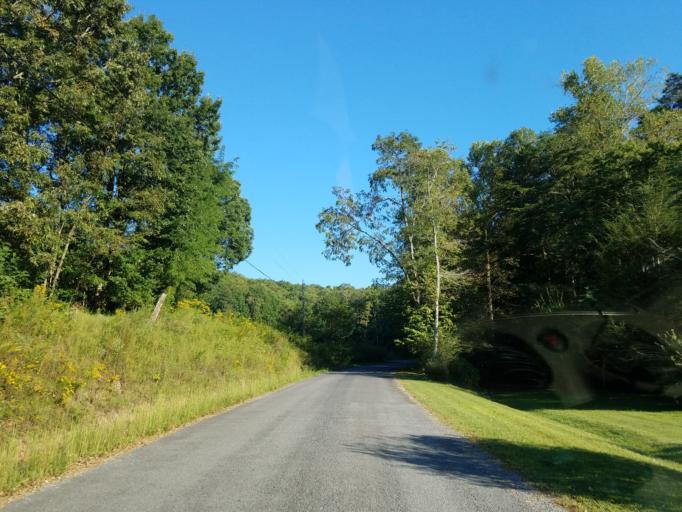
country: US
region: Georgia
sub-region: Gilmer County
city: Ellijay
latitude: 34.6452
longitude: -84.2860
